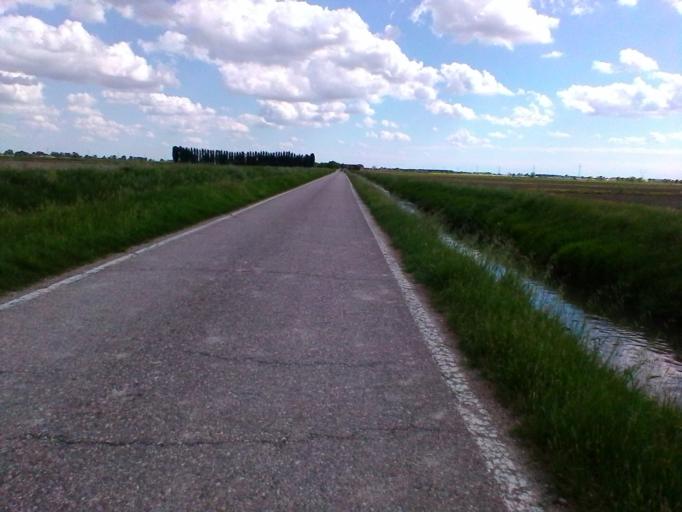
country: IT
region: Veneto
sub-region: Provincia di Verona
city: Mozzecane
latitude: 45.2818
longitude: 10.8250
